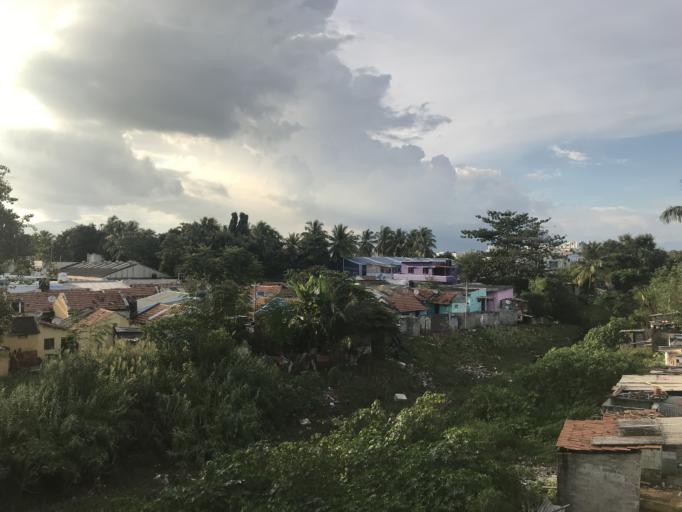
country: IN
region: Tamil Nadu
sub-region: Coimbatore
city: Coimbatore
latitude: 11.0288
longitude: 76.9550
